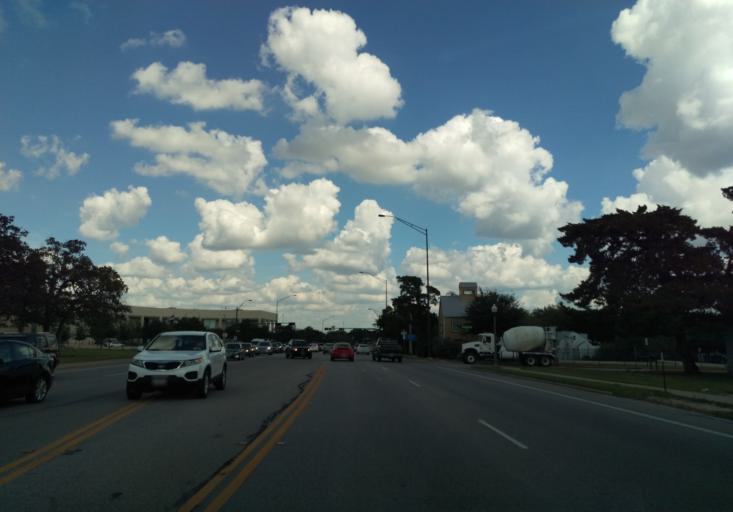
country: US
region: Texas
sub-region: Brazos County
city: College Station
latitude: 30.6064
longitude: -96.3371
